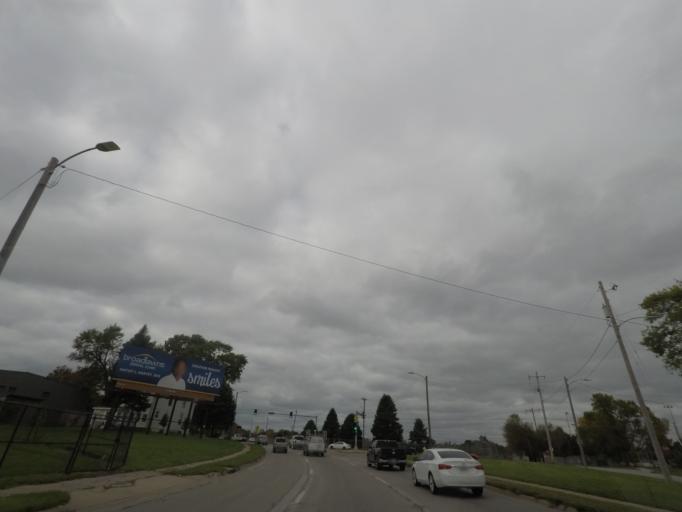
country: US
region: Iowa
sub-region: Polk County
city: Des Moines
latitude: 41.5975
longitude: -93.5967
